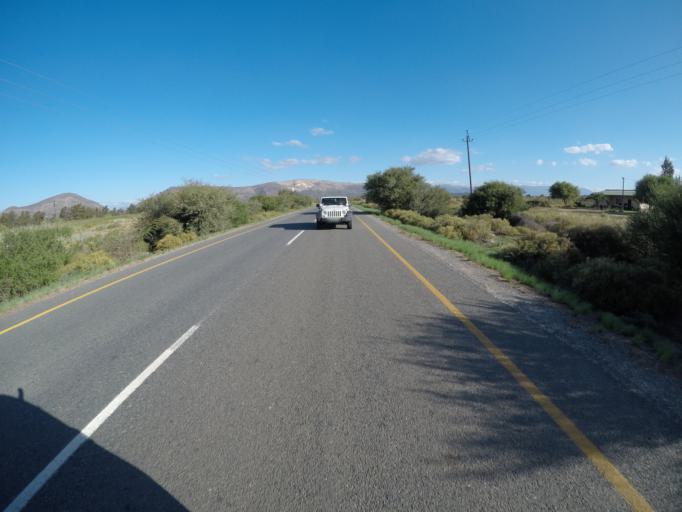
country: ZA
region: Western Cape
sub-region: Cape Winelands District Municipality
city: Ashton
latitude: -33.8023
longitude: 19.7817
